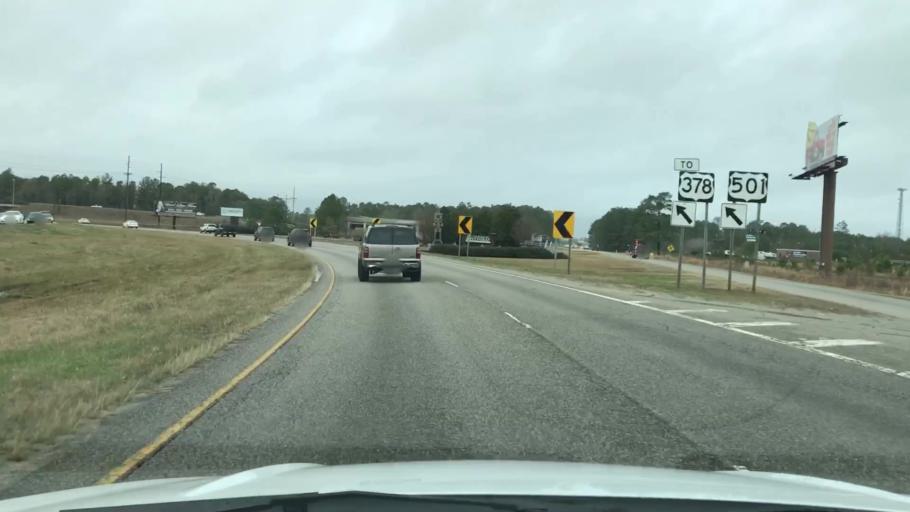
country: US
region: South Carolina
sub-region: Horry County
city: Red Hill
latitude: 33.8060
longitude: -79.0107
